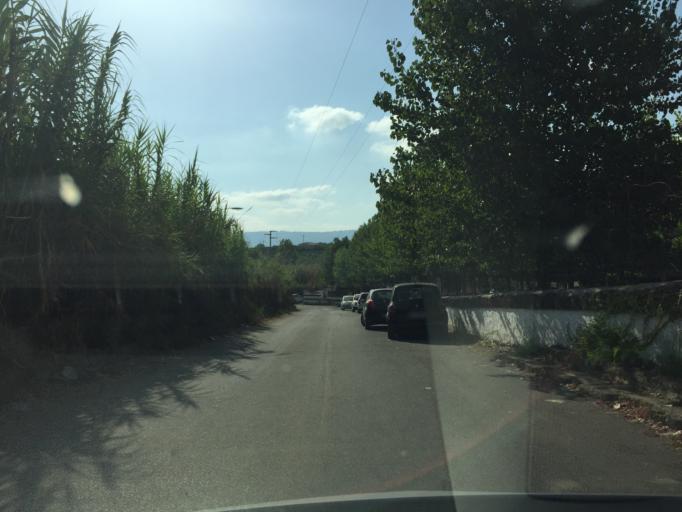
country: IT
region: Calabria
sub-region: Provincia di Vibo-Valentia
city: Briatico
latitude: 38.7209
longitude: 16.0553
